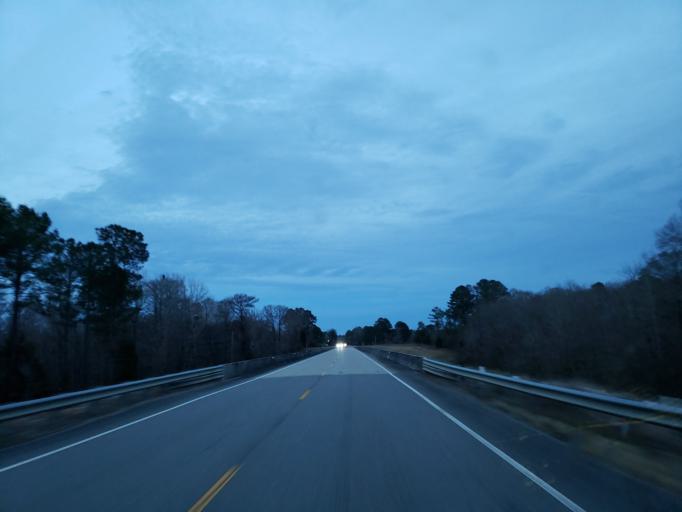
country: US
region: Alabama
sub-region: Greene County
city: Eutaw
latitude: 32.8459
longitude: -88.1230
